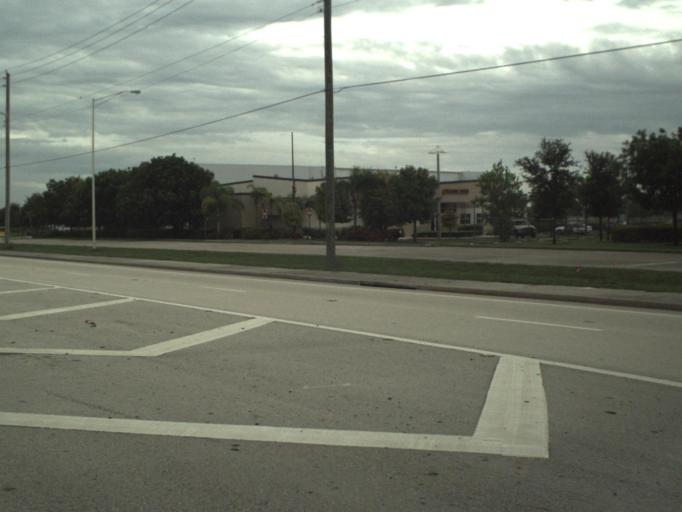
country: US
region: Florida
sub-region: Palm Beach County
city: Royal Palm Estates
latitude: 26.6778
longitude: -80.1070
